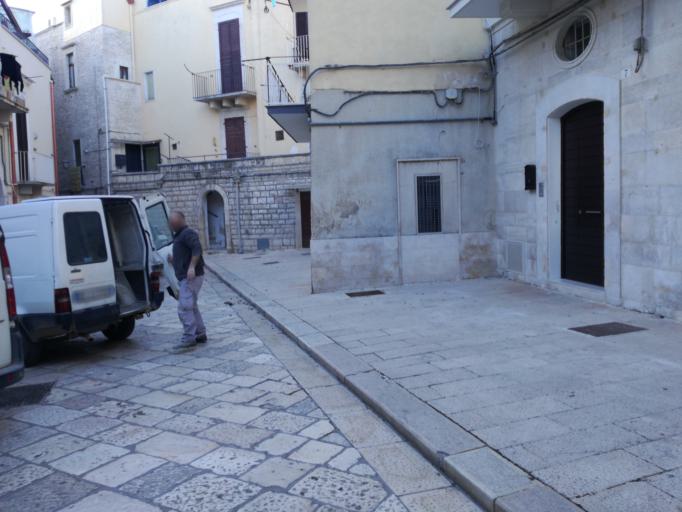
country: IT
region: Apulia
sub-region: Provincia di Bari
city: Ruvo di Puglia
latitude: 41.1156
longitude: 16.4859
